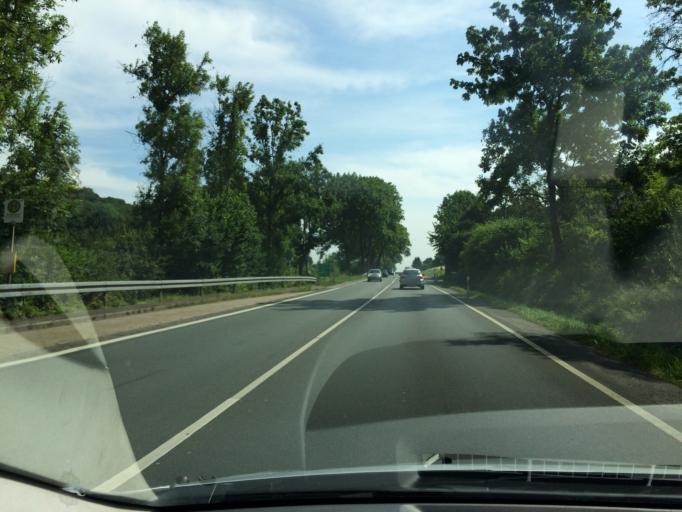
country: DE
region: North Rhine-Westphalia
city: Iserlohn
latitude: 51.3858
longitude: 7.7336
